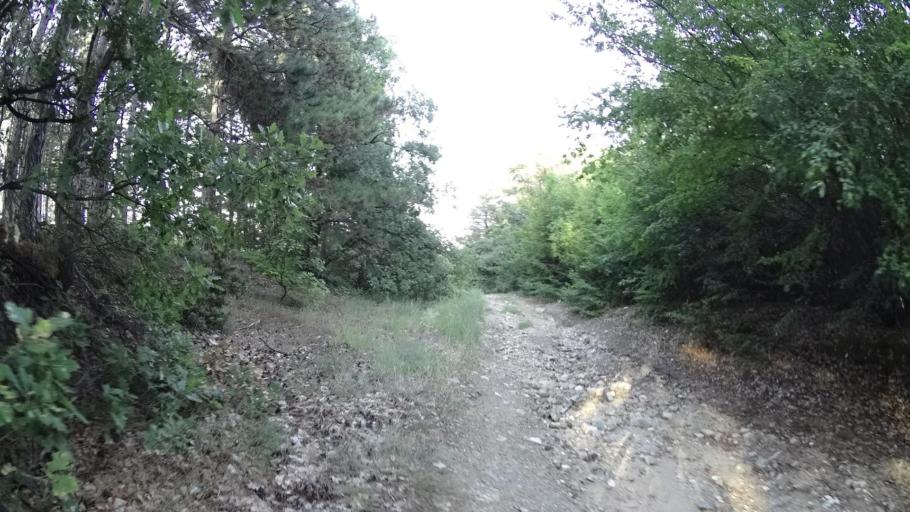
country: BG
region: Plovdiv
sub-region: Obshtina Plovdiv
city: Plovdiv
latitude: 42.0560
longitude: 24.6923
